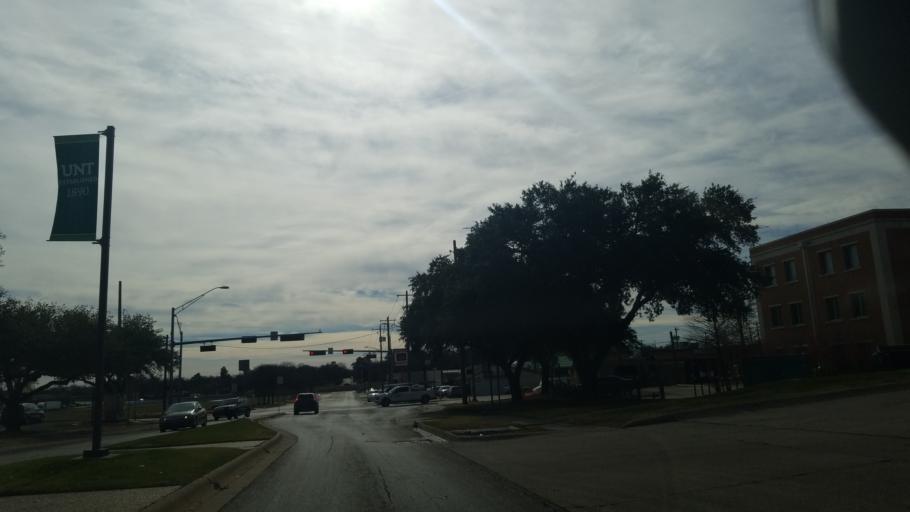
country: US
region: Texas
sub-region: Denton County
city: Denton
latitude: 33.2075
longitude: -97.1508
